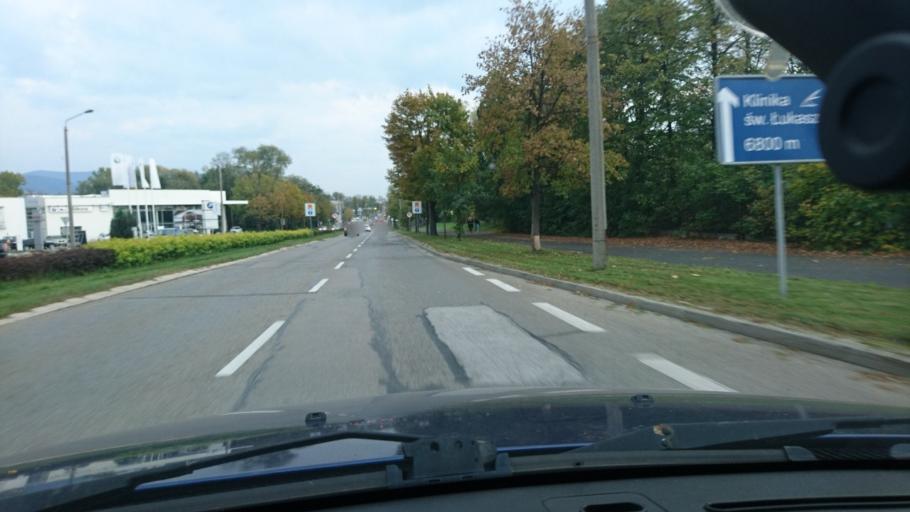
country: PL
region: Silesian Voivodeship
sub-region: Bielsko-Biala
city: Bielsko-Biala
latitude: 49.8360
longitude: 19.0407
